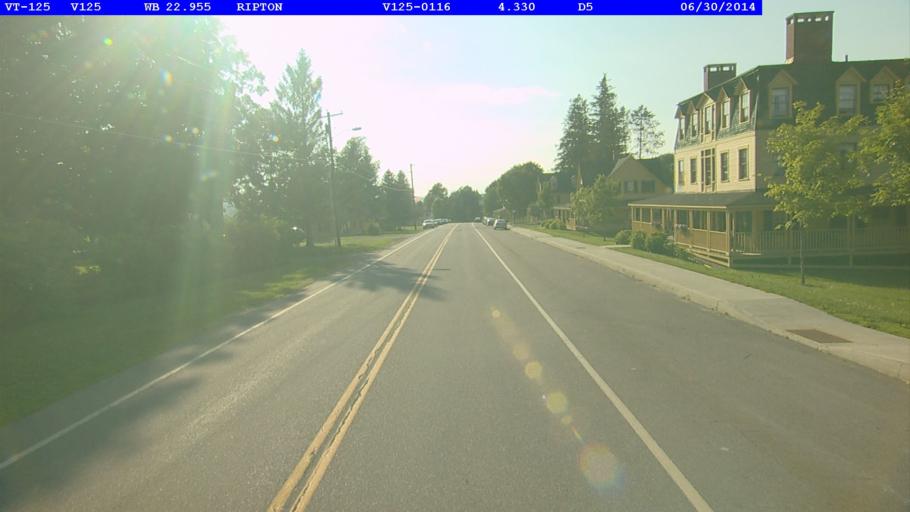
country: US
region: Vermont
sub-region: Rutland County
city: Brandon
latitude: 43.9529
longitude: -72.9916
